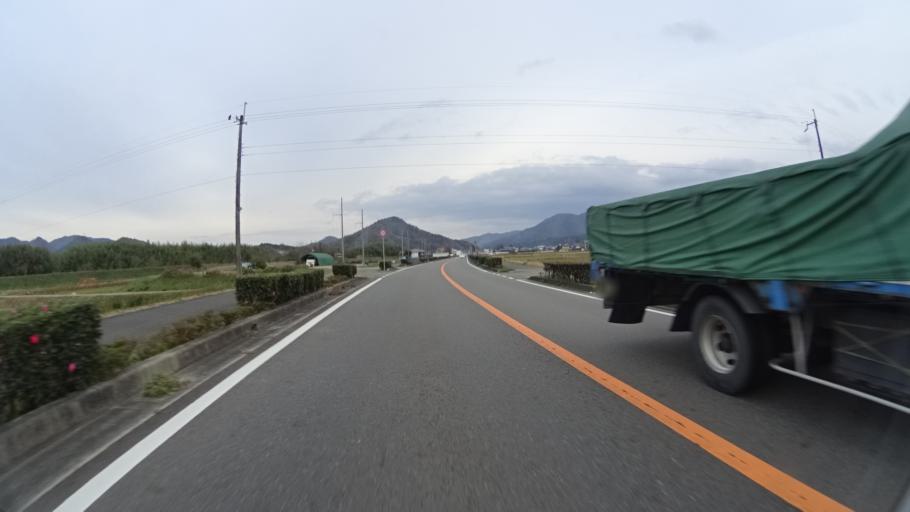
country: JP
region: Hyogo
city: Sasayama
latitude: 35.0704
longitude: 135.2680
